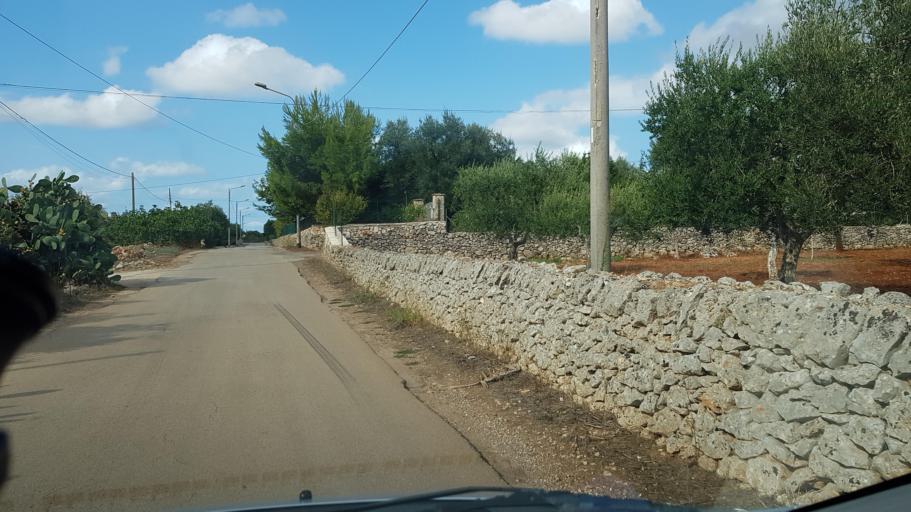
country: IT
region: Apulia
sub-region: Provincia di Brindisi
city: San Vito dei Normanni
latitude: 40.6695
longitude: 17.7172
